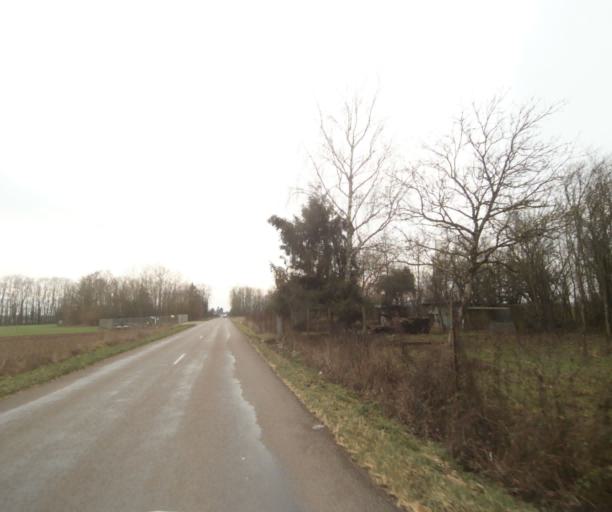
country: FR
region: Champagne-Ardenne
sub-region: Departement de la Haute-Marne
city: Villiers-en-Lieu
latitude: 48.6728
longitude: 4.8902
